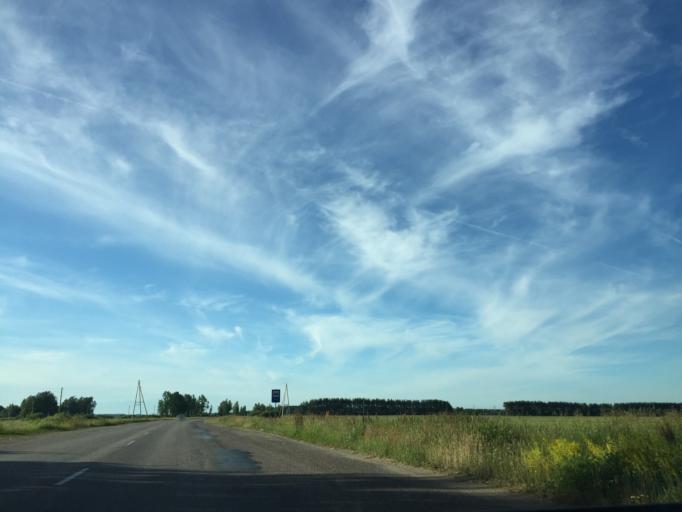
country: LV
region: Ventspils
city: Ventspils
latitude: 57.3318
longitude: 21.5639
